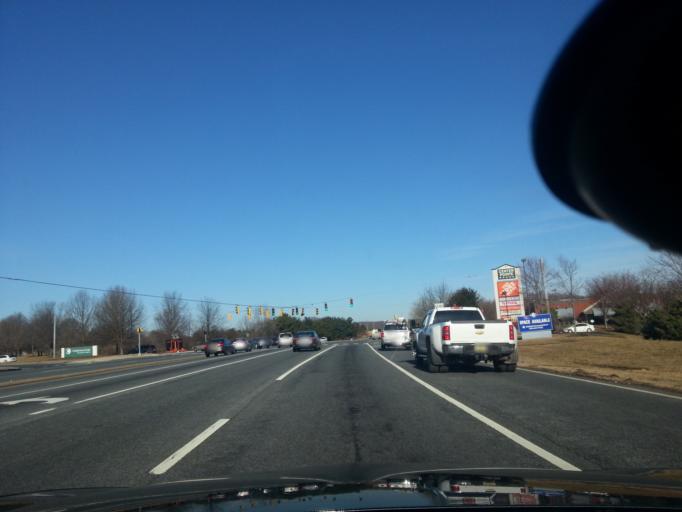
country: US
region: Delaware
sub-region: New Castle County
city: Pike Creek
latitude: 39.6903
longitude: -75.6634
